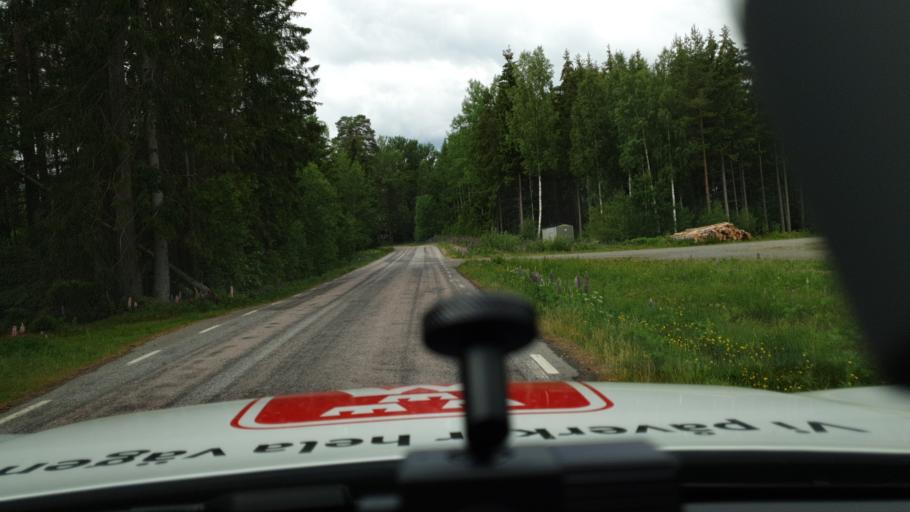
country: SE
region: Vaestra Goetaland
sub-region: Gullspangs Kommun
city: Anderstorp
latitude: 58.7989
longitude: 14.2711
